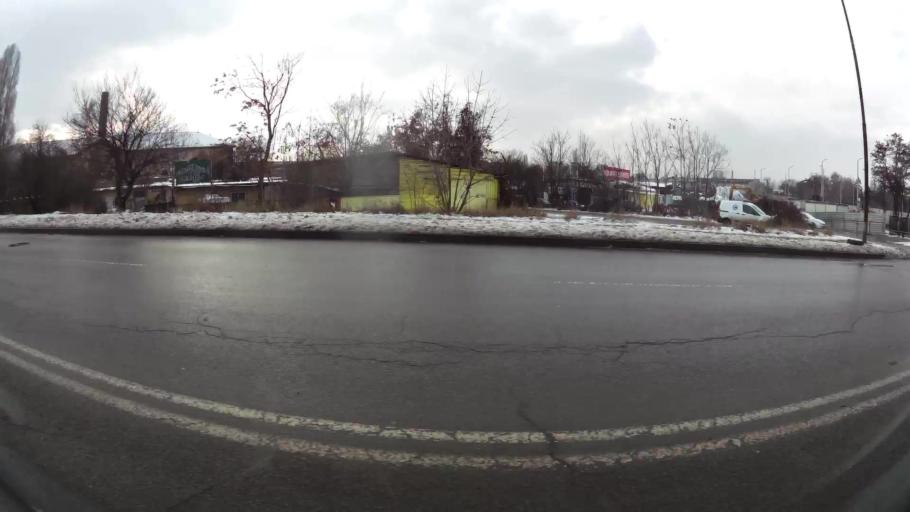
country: BG
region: Sofia-Capital
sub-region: Stolichna Obshtina
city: Sofia
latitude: 42.7014
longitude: 23.3510
